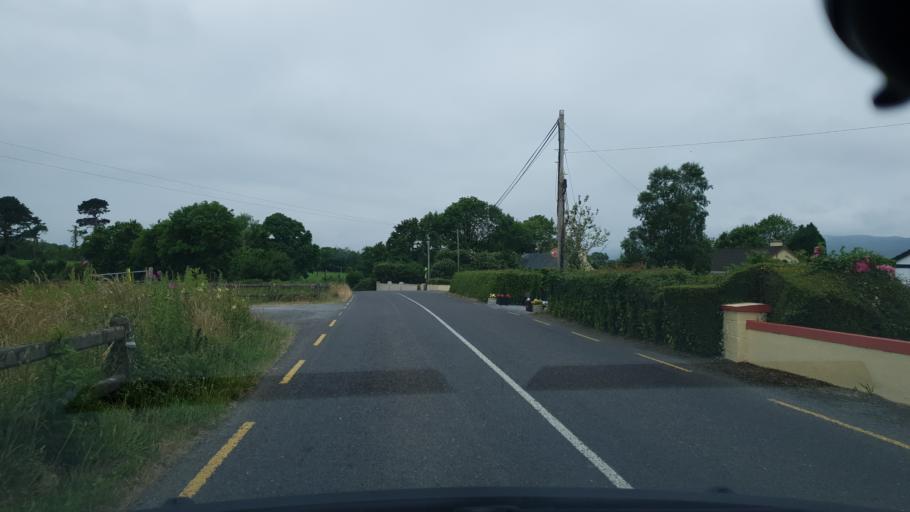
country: IE
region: Munster
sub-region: Ciarrai
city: Tralee
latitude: 52.1638
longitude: -9.6344
